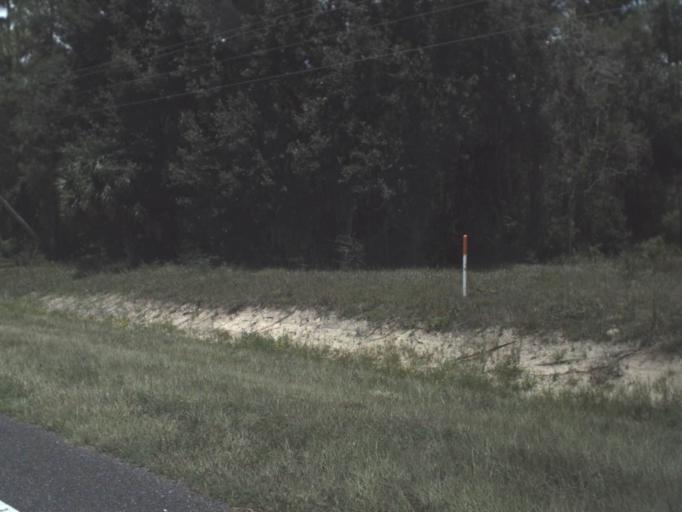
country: US
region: Florida
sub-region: Taylor County
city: Perry
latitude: 30.0214
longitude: -83.5332
